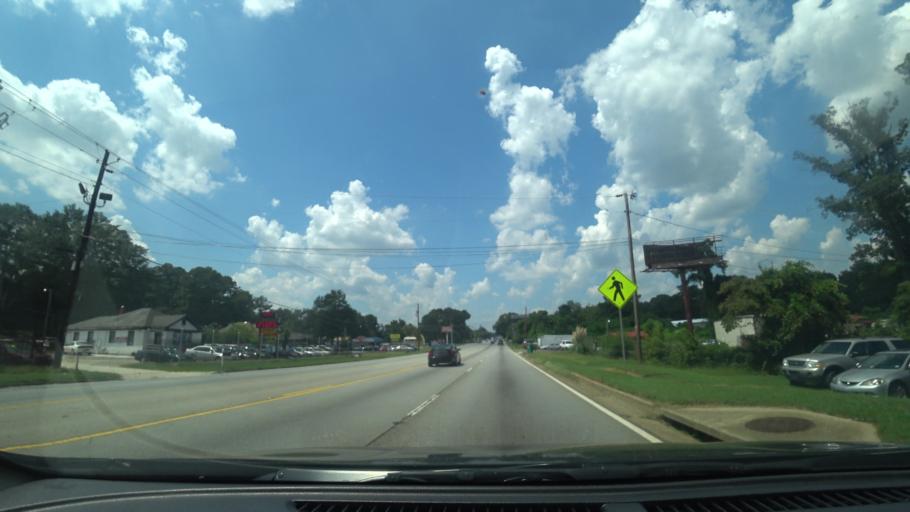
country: US
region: Georgia
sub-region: DeKalb County
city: Belvedere Park
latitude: 33.7489
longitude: -84.2241
